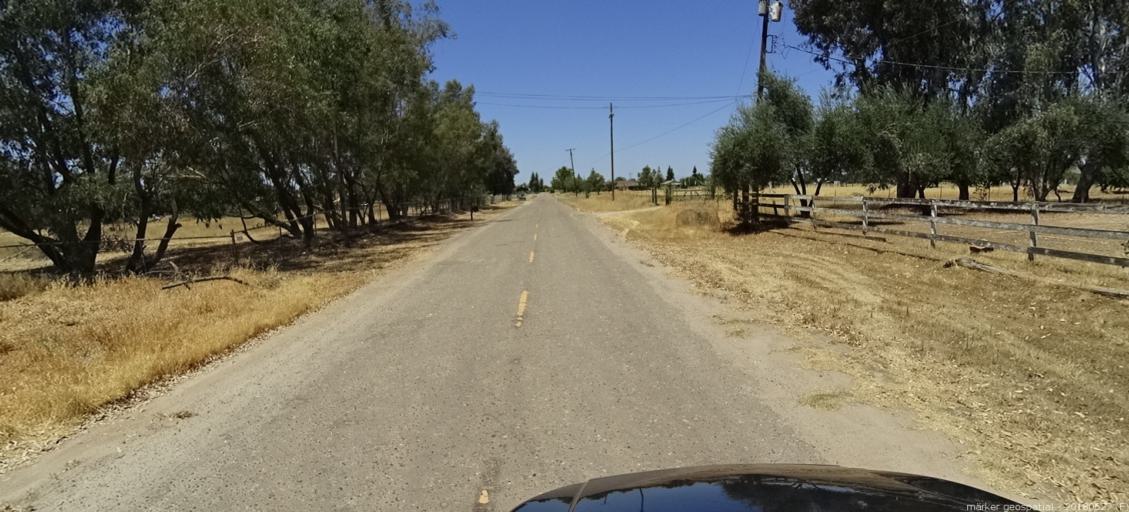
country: US
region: California
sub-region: Madera County
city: Bonadelle Ranchos-Madera Ranchos
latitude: 36.9241
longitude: -119.9162
